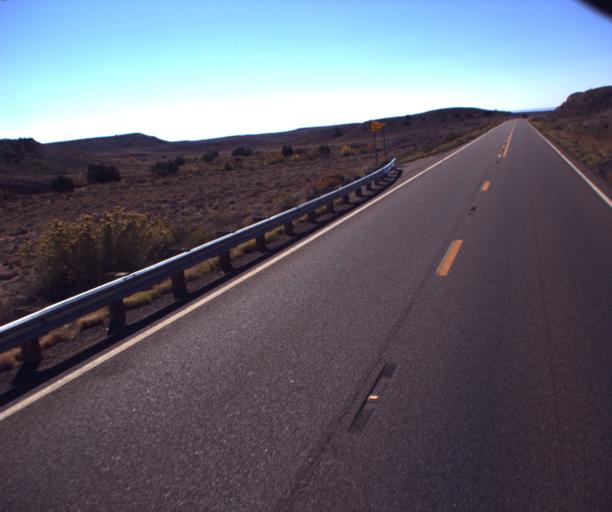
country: US
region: Arizona
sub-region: Navajo County
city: Dilkon
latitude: 35.1814
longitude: -110.4429
